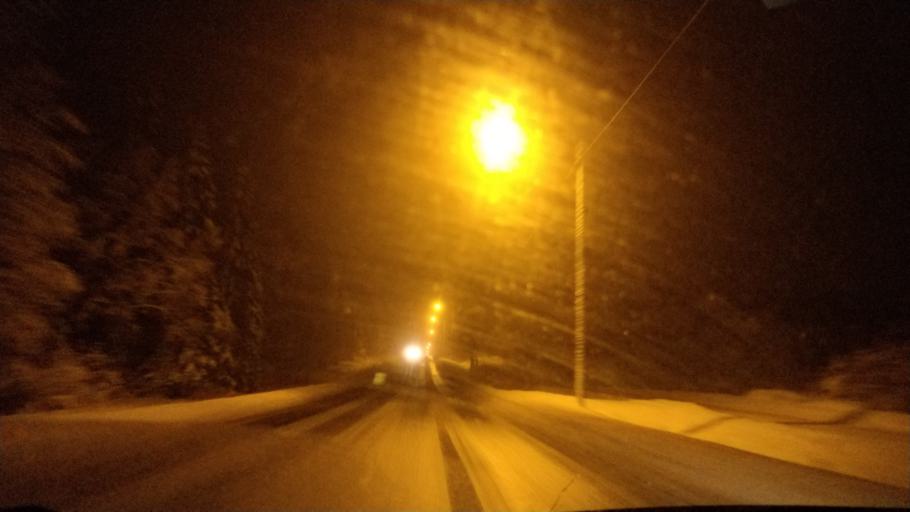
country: FI
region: Lapland
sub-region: Rovaniemi
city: Rovaniemi
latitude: 66.4273
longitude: 25.4250
